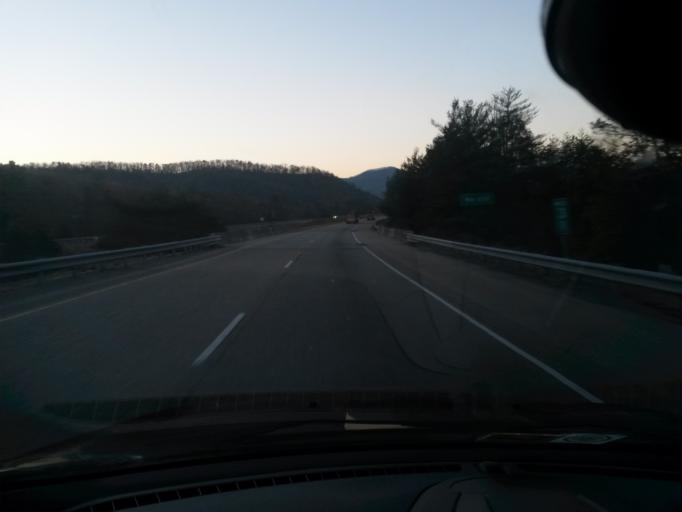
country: US
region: Virginia
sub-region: Alleghany County
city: Clifton Forge
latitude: 37.8180
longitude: -79.7420
